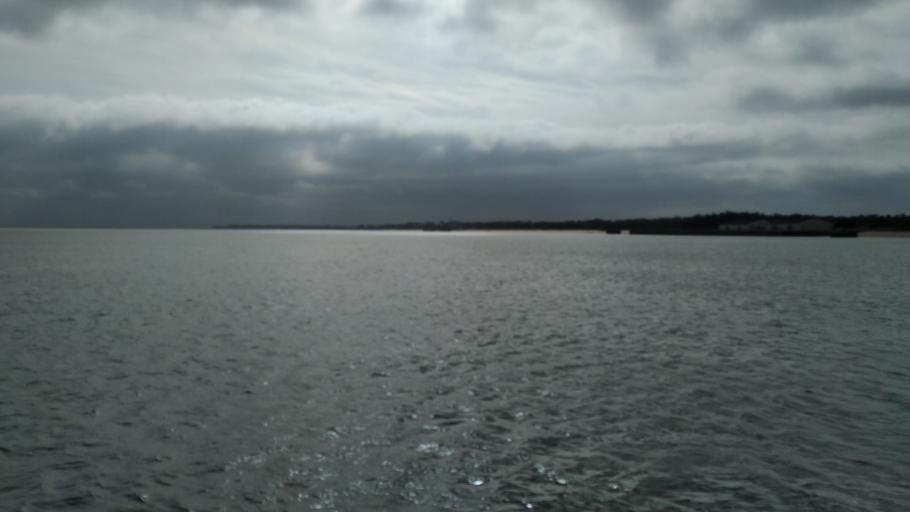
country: PT
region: Setubal
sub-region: Setubal
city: Setubal
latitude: 38.4811
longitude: -8.8711
